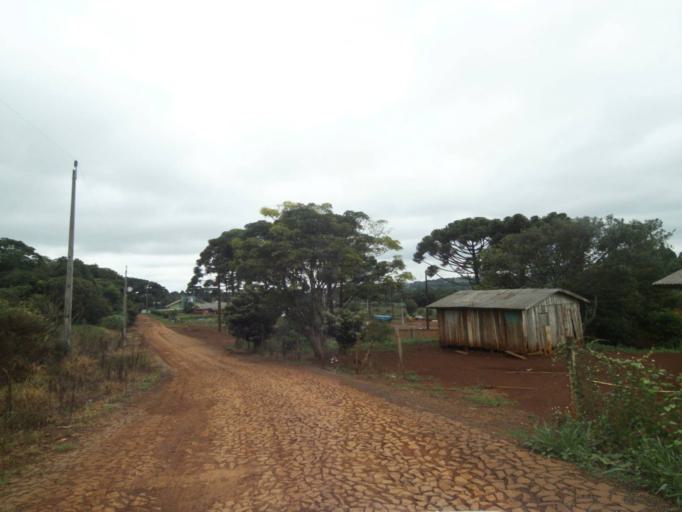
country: BR
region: Parana
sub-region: Pitanga
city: Pitanga
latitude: -24.9264
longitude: -51.8720
